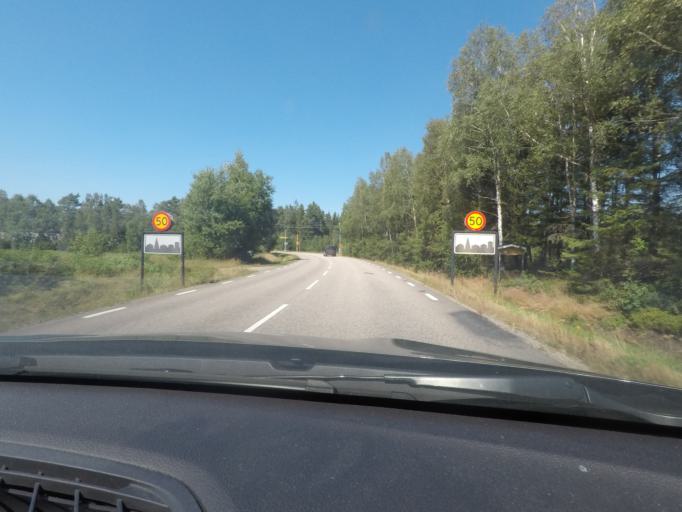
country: SE
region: Kronoberg
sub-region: Markaryds Kommun
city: Markaryd
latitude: 56.4834
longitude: 13.5328
